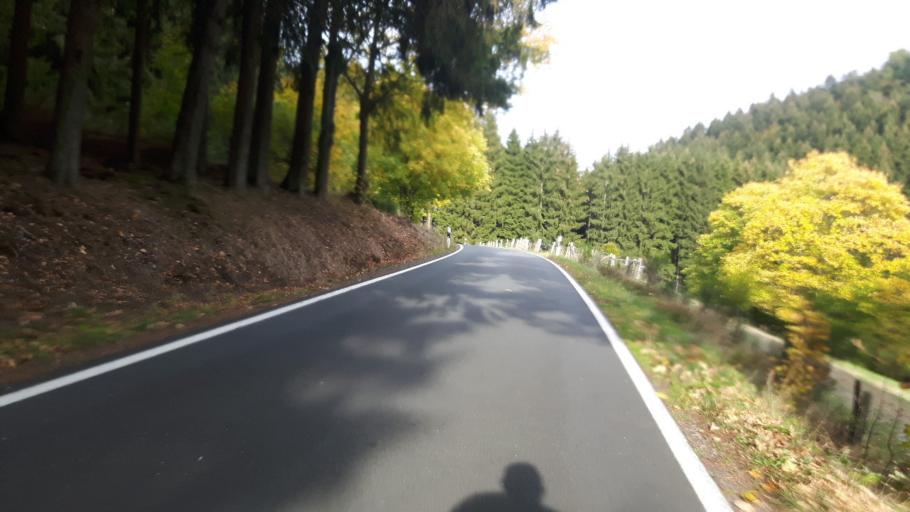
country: DE
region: North Rhine-Westphalia
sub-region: Regierungsbezirk Arnsberg
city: Erndtebruck
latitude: 50.9029
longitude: 8.3053
